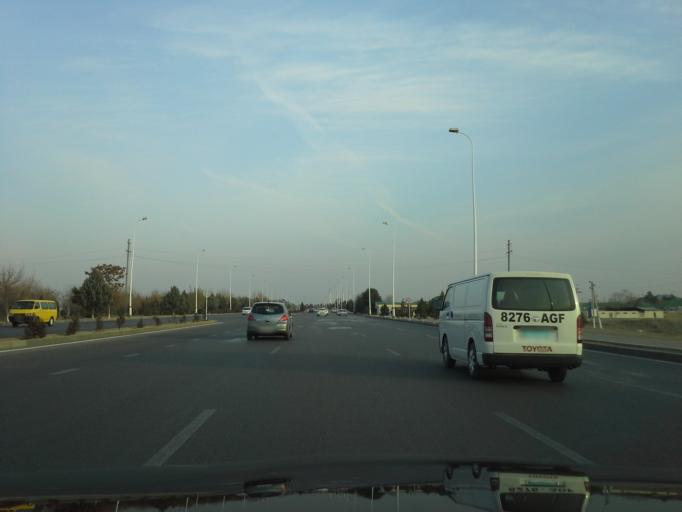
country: TM
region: Ahal
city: Abadan
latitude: 38.0329
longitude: 58.2257
